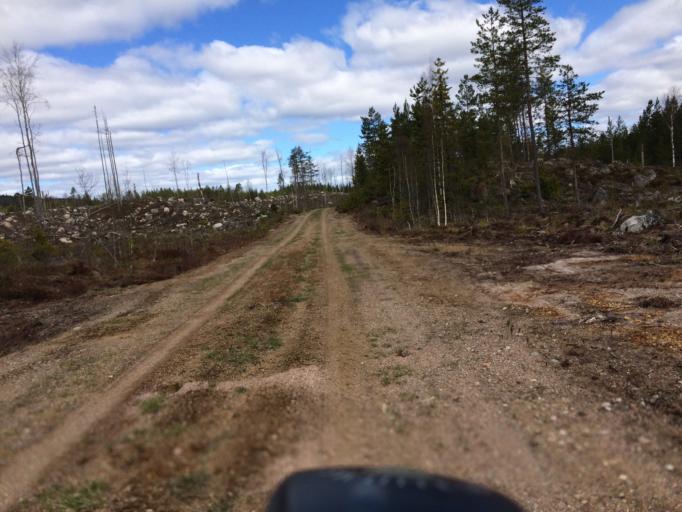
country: SE
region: OErebro
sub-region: Hallefors Kommun
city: Haellefors
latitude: 60.0511
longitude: 14.5244
